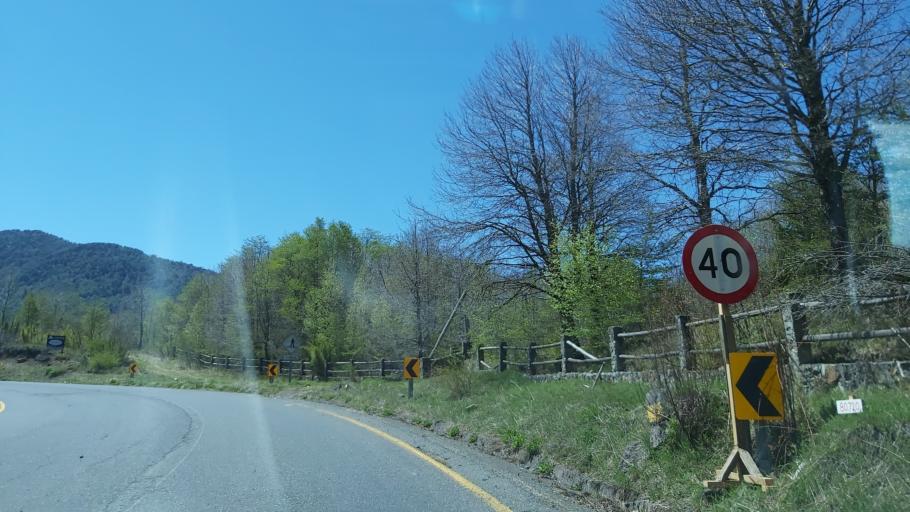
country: CL
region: Araucania
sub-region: Provincia de Cautin
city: Vilcun
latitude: -38.4666
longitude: -71.6385
